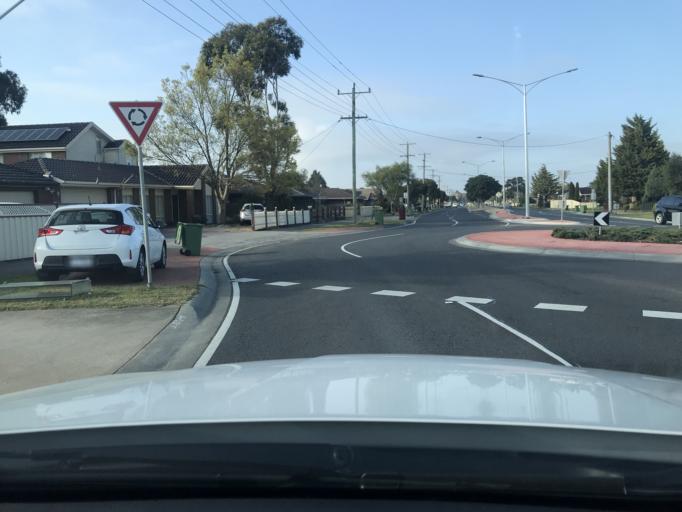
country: AU
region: Victoria
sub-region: Hume
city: Roxburgh Park
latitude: -37.6063
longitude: 144.9287
